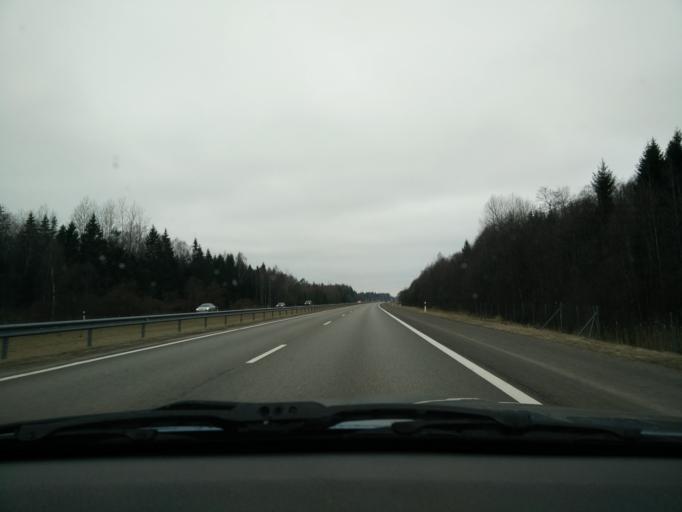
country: LT
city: Rietavas
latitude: 55.6155
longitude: 22.0124
